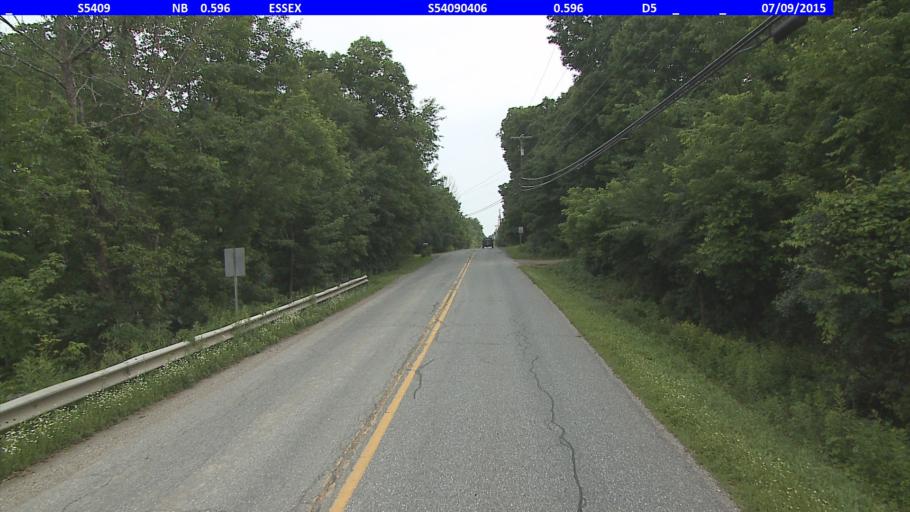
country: US
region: Vermont
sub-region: Chittenden County
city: Essex Junction
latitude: 44.5184
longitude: -73.0809
